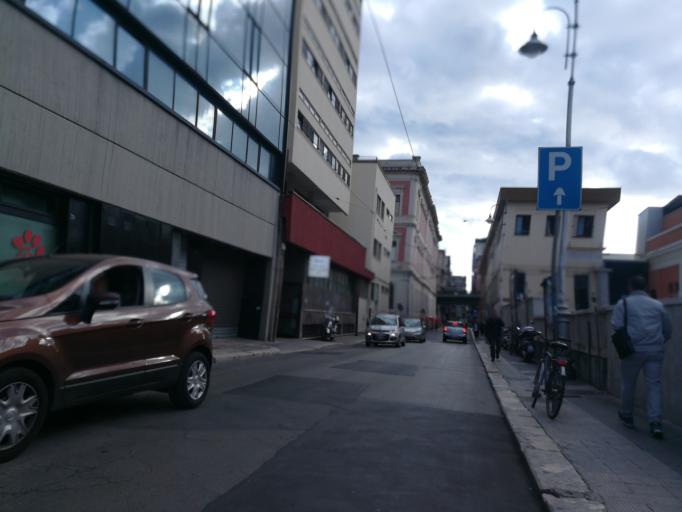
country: IT
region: Apulia
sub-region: Provincia di Bari
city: Bari
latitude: 41.1182
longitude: 16.8712
